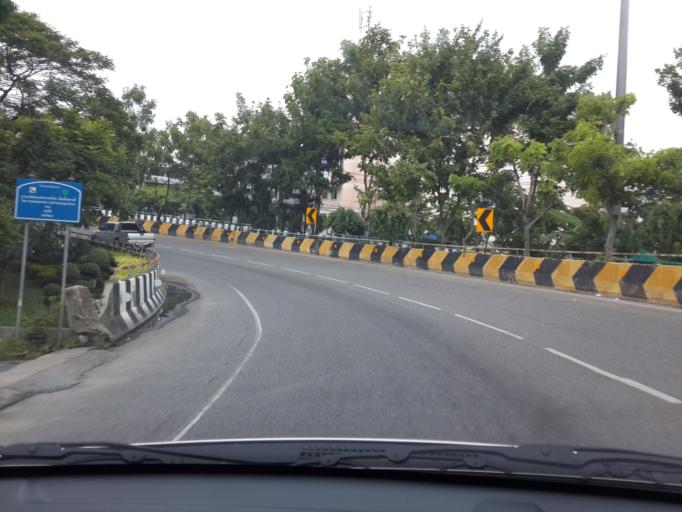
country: TH
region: Bangkok
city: Watthana
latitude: 13.7415
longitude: 100.5903
